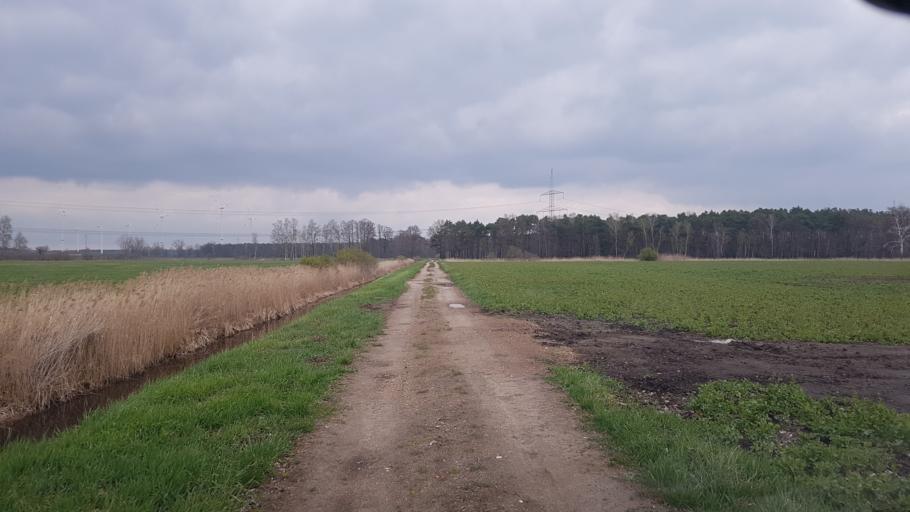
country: DE
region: Brandenburg
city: Sallgast
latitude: 51.6269
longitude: 13.8753
